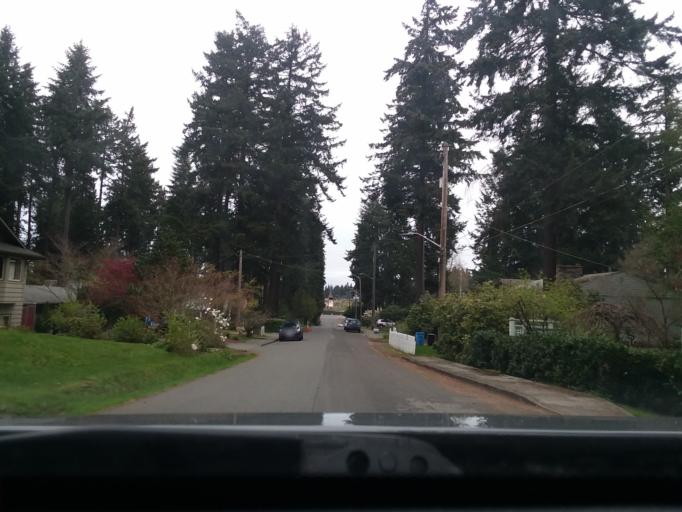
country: US
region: Washington
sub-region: King County
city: Shoreline
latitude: 47.7393
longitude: -122.3476
